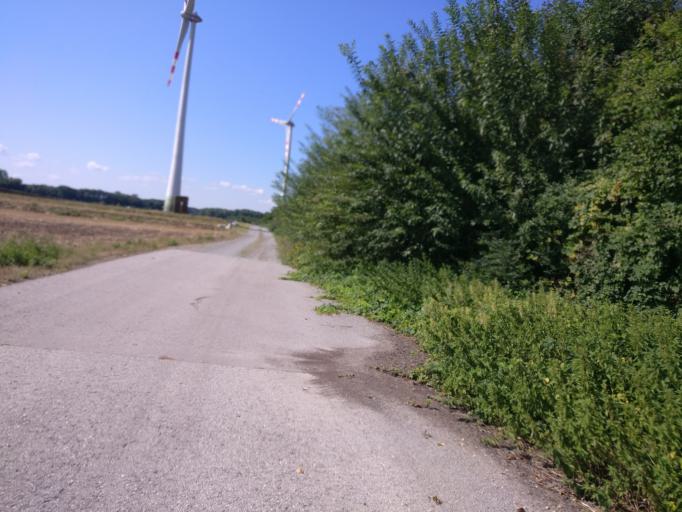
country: AT
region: Lower Austria
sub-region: Politischer Bezirk Baden
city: Ebreichsdorf
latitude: 47.9376
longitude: 16.3757
